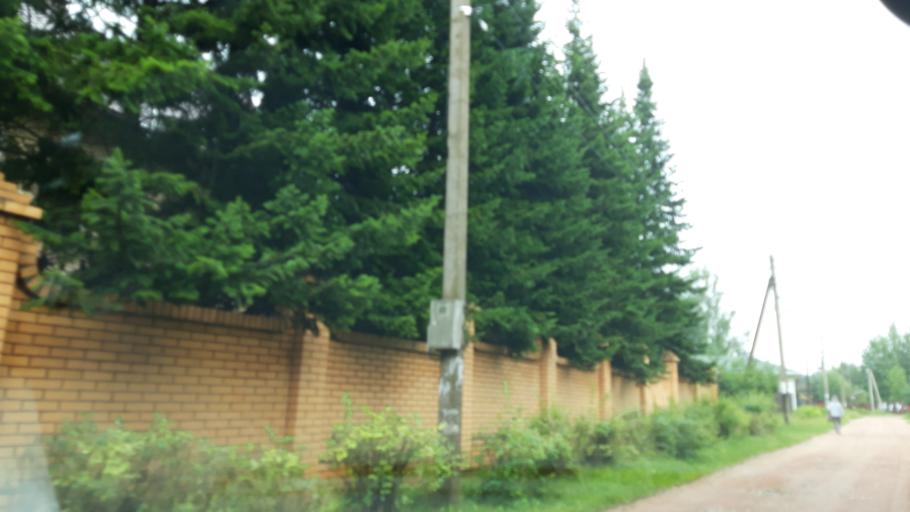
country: RU
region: Tverskaya
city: Konakovo
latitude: 56.6598
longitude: 36.6548
